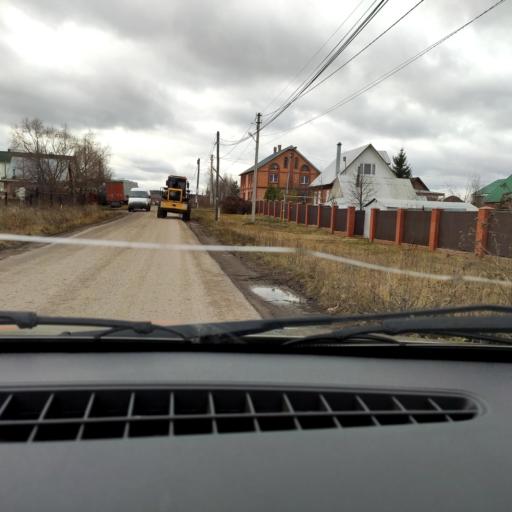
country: RU
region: Bashkortostan
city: Avdon
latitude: 54.4926
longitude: 55.8635
